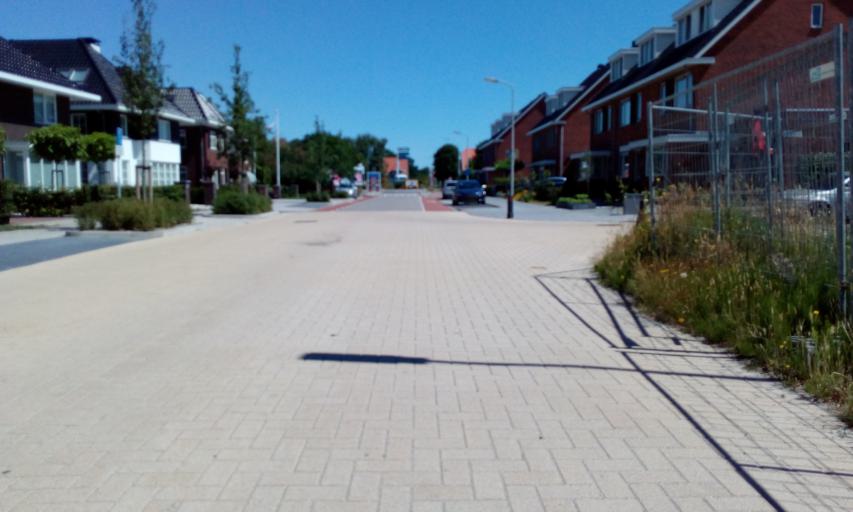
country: NL
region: South Holland
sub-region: Gemeente Teylingen
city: Voorhout
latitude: 52.2305
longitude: 4.4931
